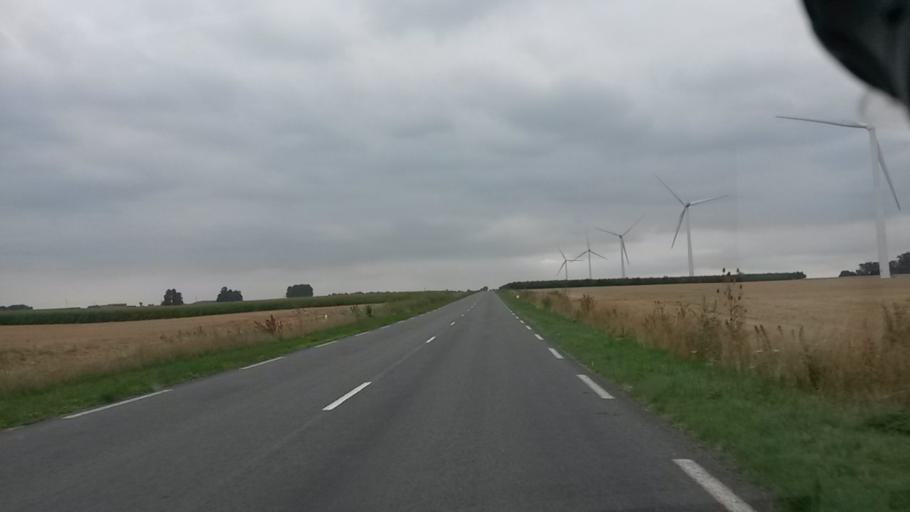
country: FR
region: Haute-Normandie
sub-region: Departement de la Seine-Maritime
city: Aumale
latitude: 49.7717
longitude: 1.8389
